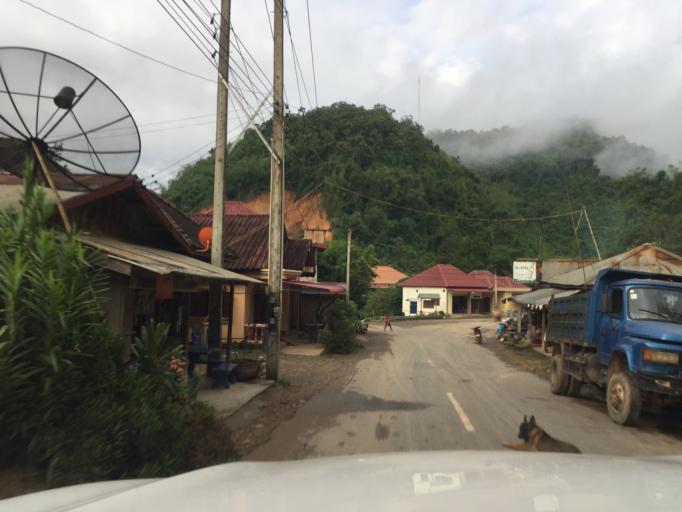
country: LA
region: Phongsali
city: Khoa
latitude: 21.1022
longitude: 102.2545
